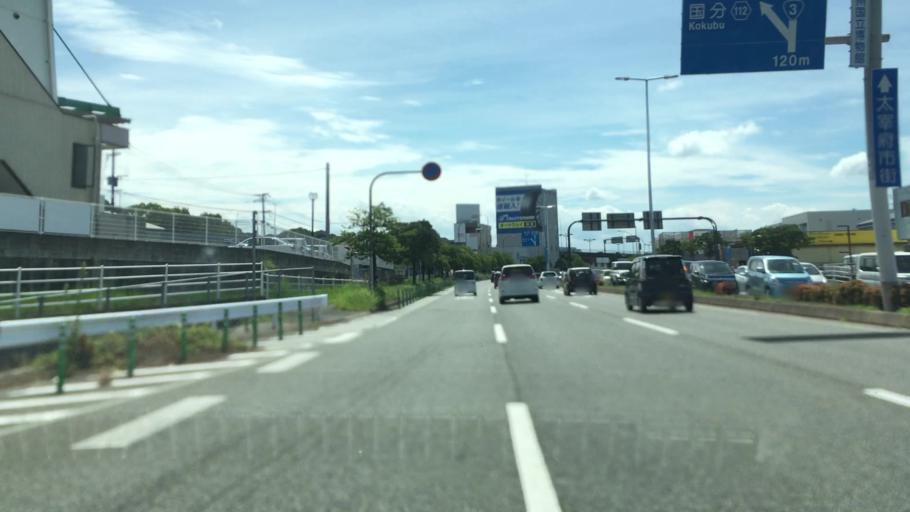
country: JP
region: Fukuoka
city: Onojo
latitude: 33.5288
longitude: 130.4939
